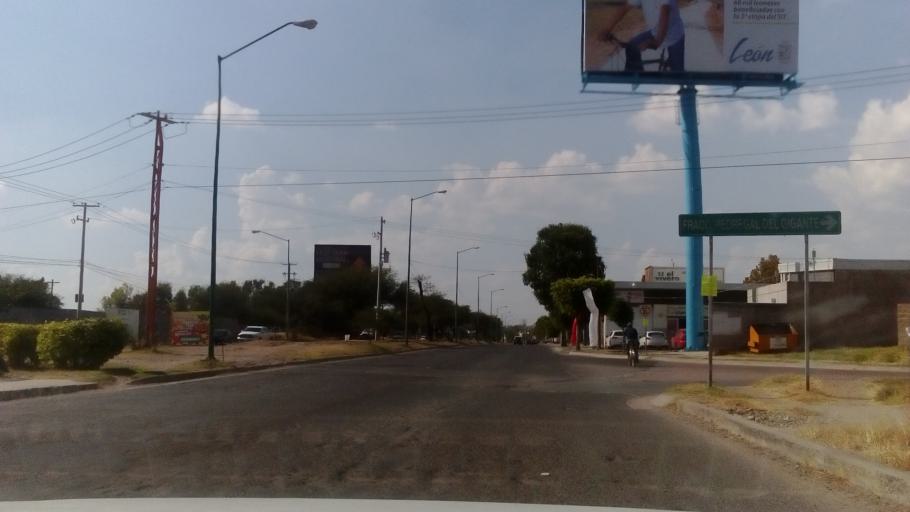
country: MX
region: Guanajuato
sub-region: Leon
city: Medina
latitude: 21.1231
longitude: -101.6168
